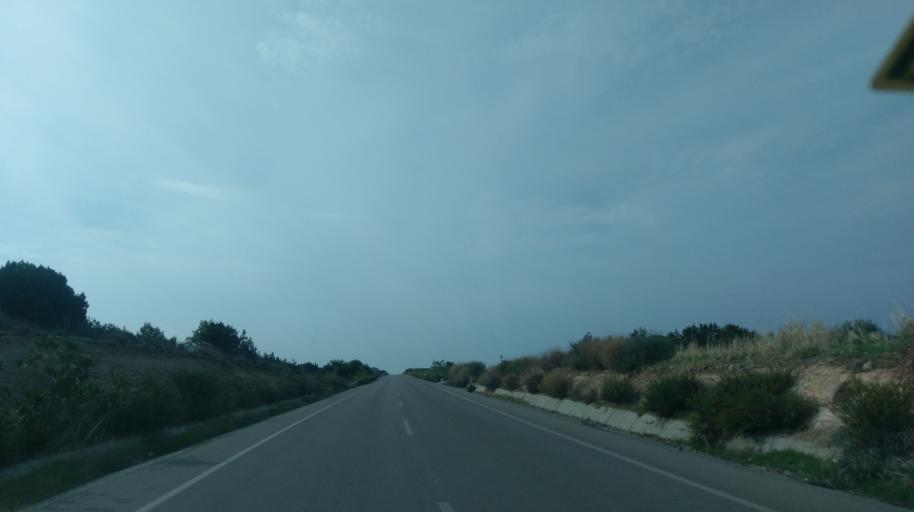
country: CY
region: Ammochostos
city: Trikomo
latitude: 35.4307
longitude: 33.9316
